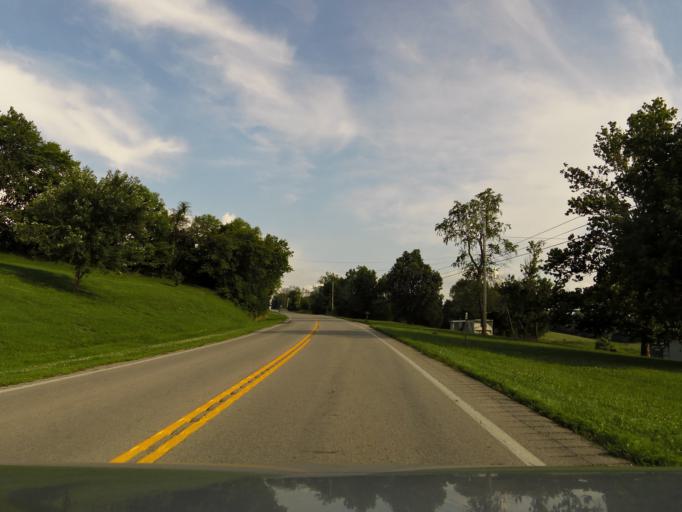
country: US
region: Kentucky
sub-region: Harrison County
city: Cynthiana
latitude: 38.3379
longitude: -84.3073
